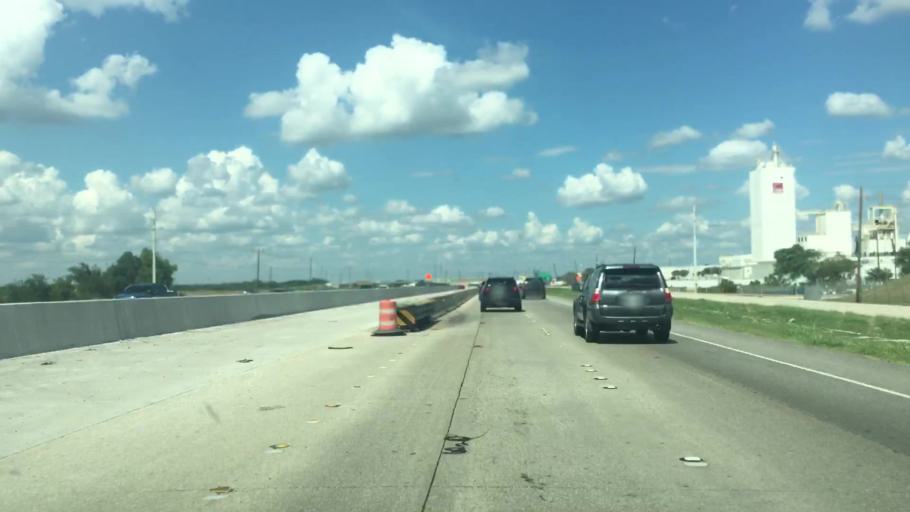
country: US
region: Texas
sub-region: Ellis County
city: Waxahachie
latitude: 32.4375
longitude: -96.8532
